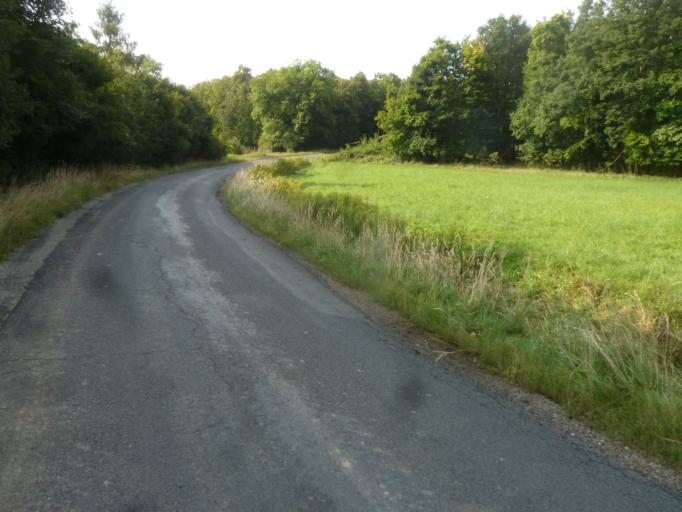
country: HU
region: Veszprem
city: Urkut
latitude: 47.0596
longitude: 17.6719
